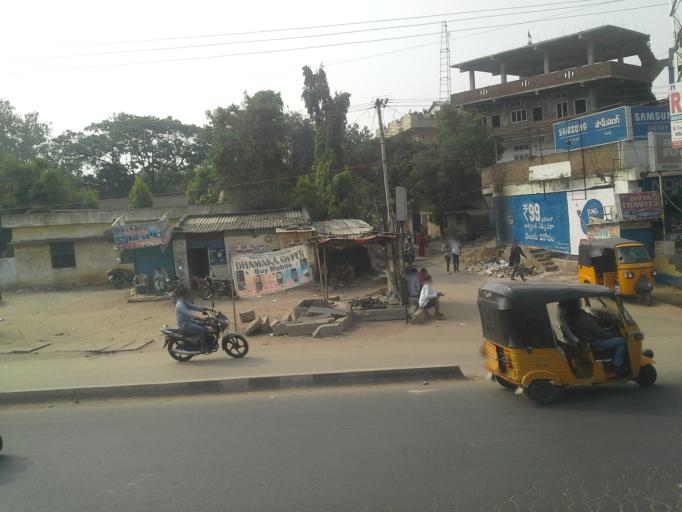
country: IN
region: Telangana
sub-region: Medak
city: Patancheru
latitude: 17.5292
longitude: 78.2655
